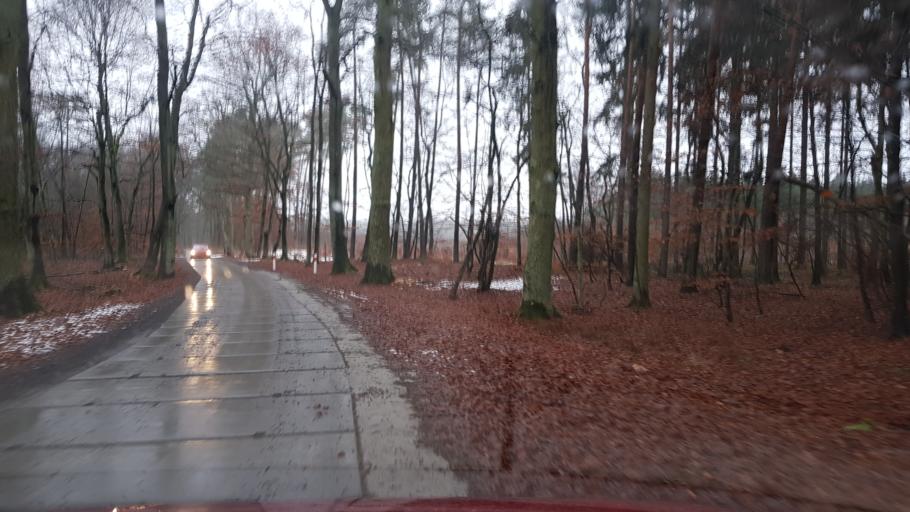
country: PL
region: West Pomeranian Voivodeship
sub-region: Powiat policki
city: Dobra
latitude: 53.5511
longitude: 14.4118
